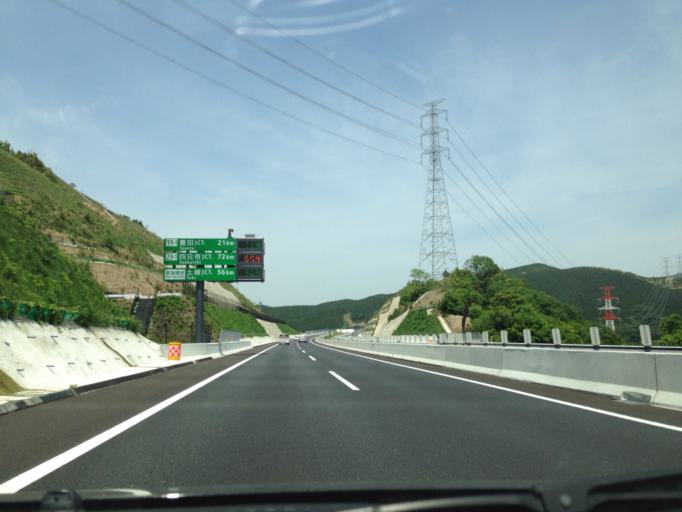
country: JP
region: Aichi
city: Okazaki
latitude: 34.9296
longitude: 137.2661
